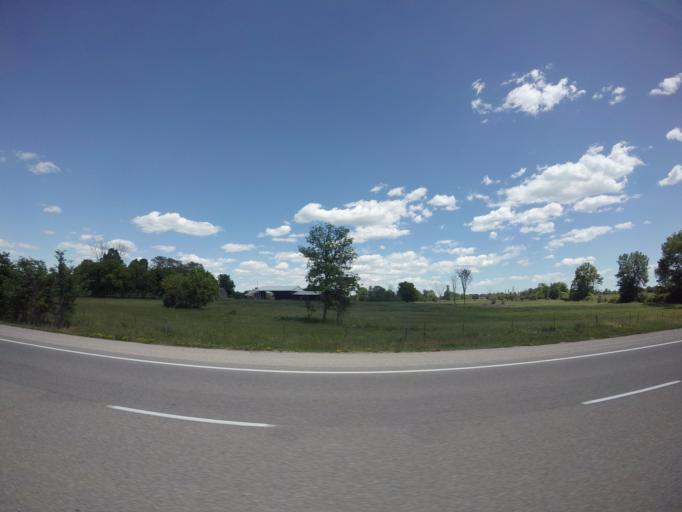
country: CA
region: Ontario
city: Perth
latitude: 44.9760
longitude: -76.2270
